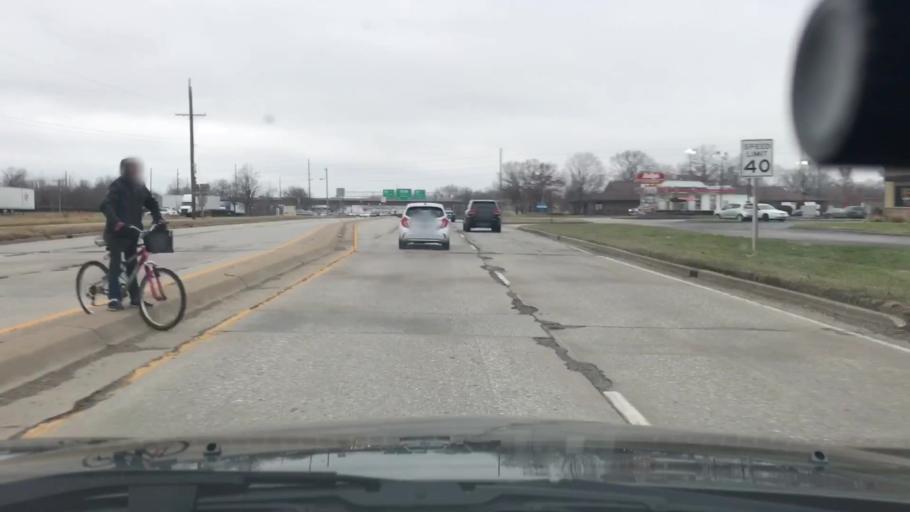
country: US
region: Illinois
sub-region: Madison County
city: Bethalto
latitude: 38.9014
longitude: -90.0603
